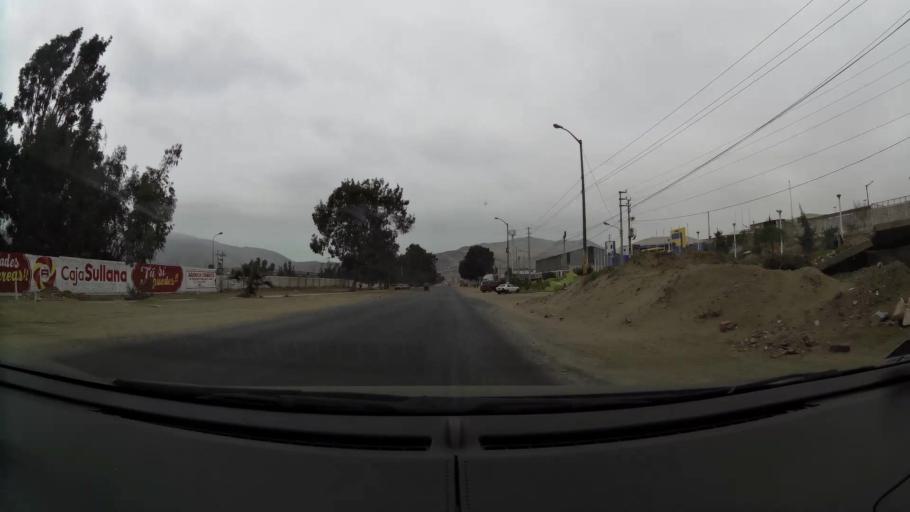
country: PE
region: Ancash
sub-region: Provincia de Santa
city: Chimbote
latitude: -9.0544
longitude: -78.5918
